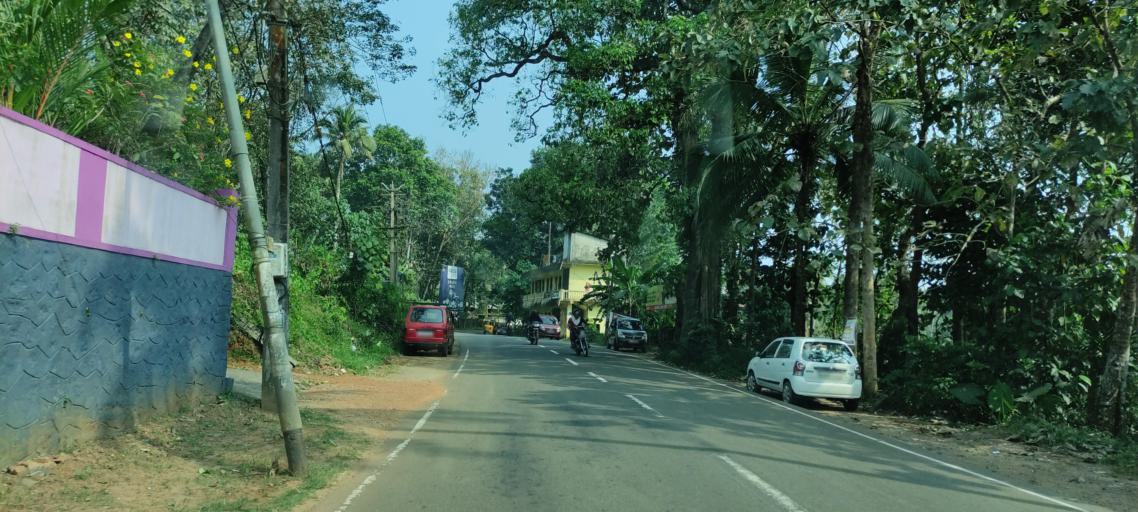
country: IN
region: Kerala
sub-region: Pattanamtitta
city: Pathanamthitta
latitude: 9.2320
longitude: 76.7468
